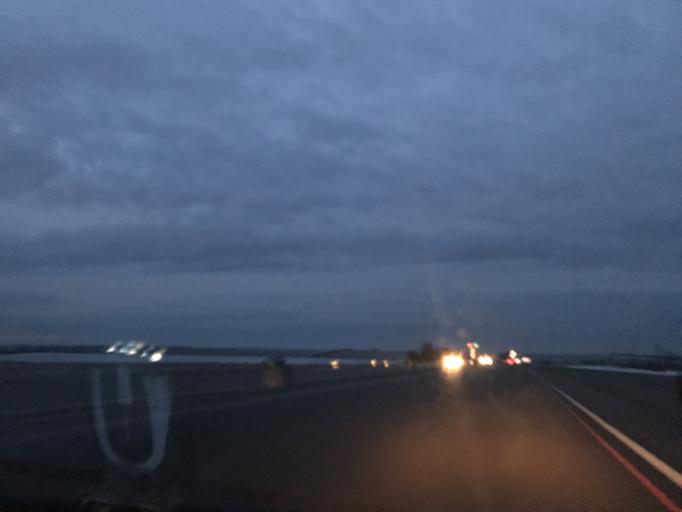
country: RU
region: Rostov
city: Samarskoye
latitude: 47.0118
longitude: 39.7335
